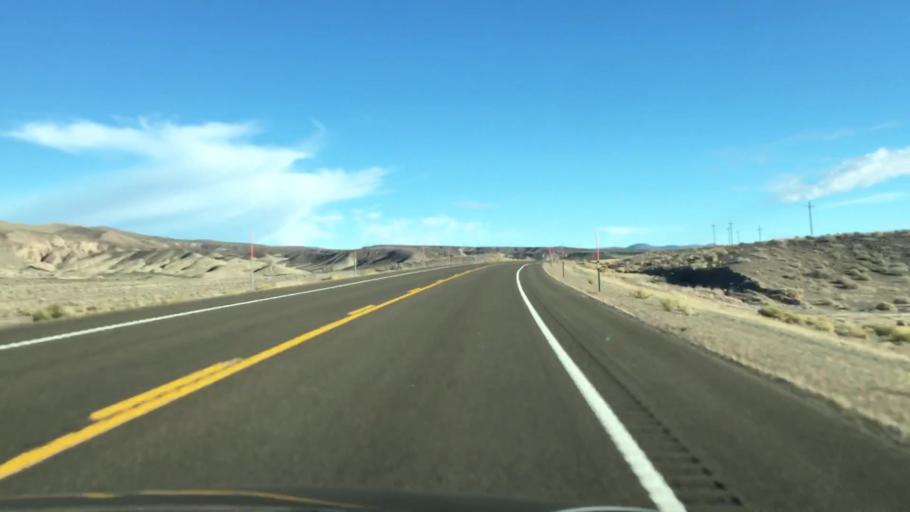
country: US
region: Nevada
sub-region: Mineral County
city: Hawthorne
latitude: 38.2364
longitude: -118.0286
